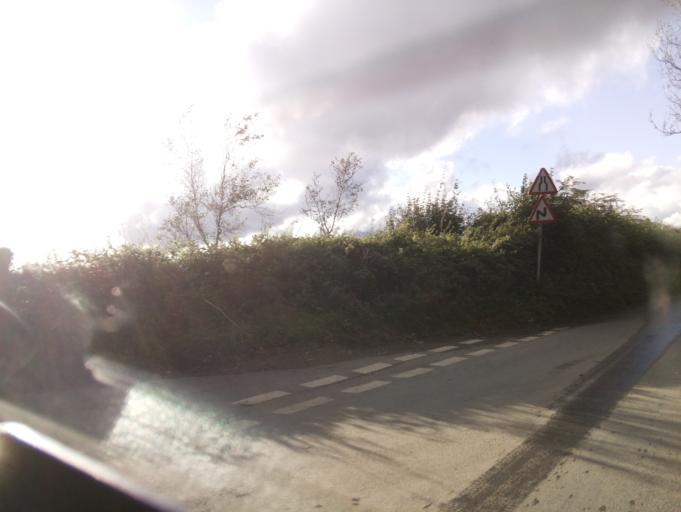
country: GB
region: England
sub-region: Devon
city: Totnes
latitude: 50.3687
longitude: -3.7424
